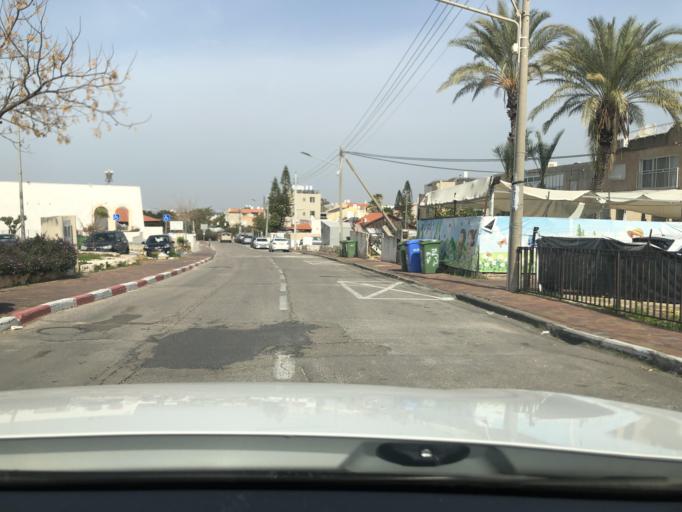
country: IL
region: Central District
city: Rosh Ha'Ayin
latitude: 32.0908
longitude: 34.9601
